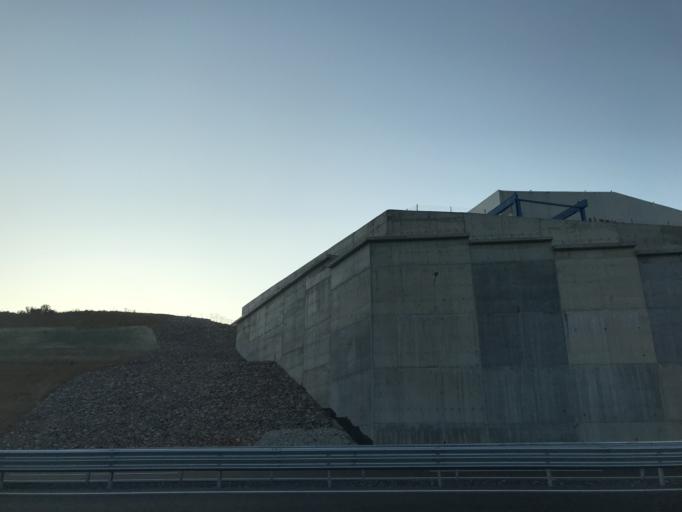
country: TR
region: Kocaeli
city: Tavsanli
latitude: 40.8041
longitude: 29.5199
